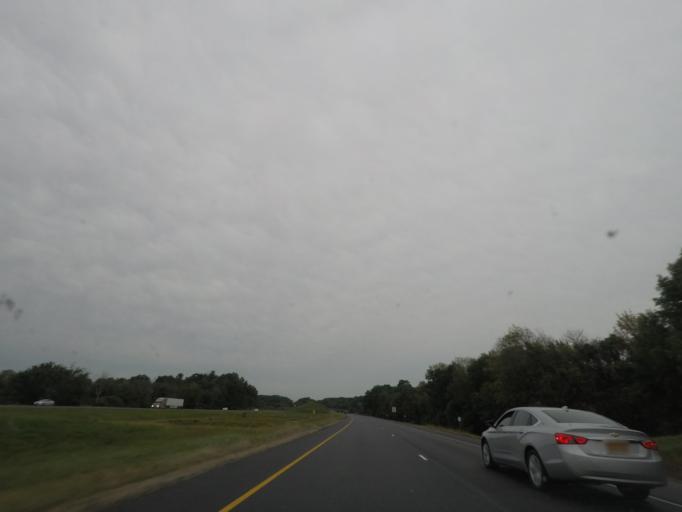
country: US
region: New York
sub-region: Rensselaer County
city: Nassau
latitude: 42.4839
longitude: -73.6383
